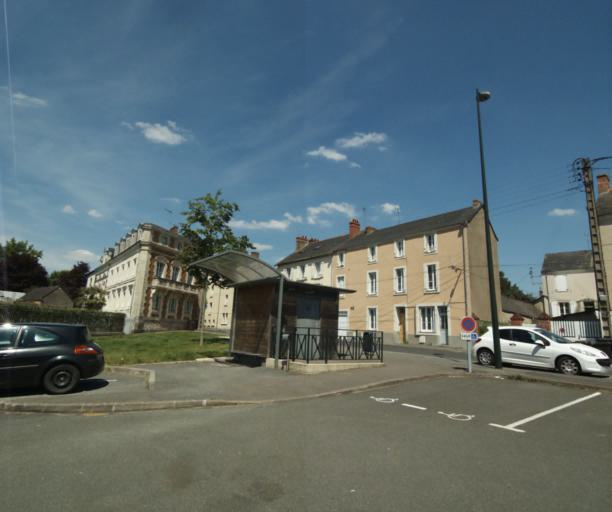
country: FR
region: Pays de la Loire
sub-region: Departement de la Mayenne
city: Laval
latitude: 48.0783
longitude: -0.7698
